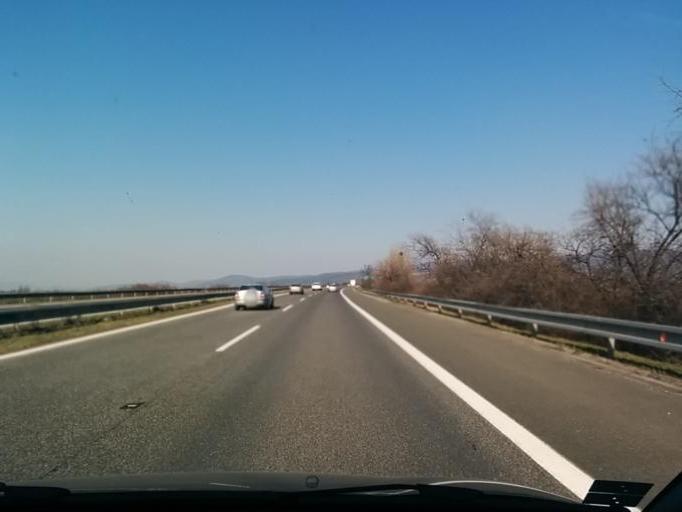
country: SK
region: Trnavsky
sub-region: Okres Trnava
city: Piestany
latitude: 48.6422
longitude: 17.8181
